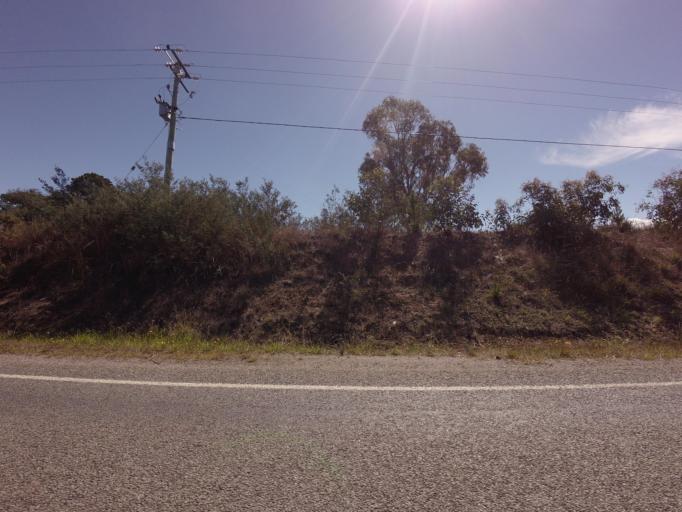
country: AU
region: Tasmania
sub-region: Northern Midlands
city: Evandale
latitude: -41.7858
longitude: 147.7166
